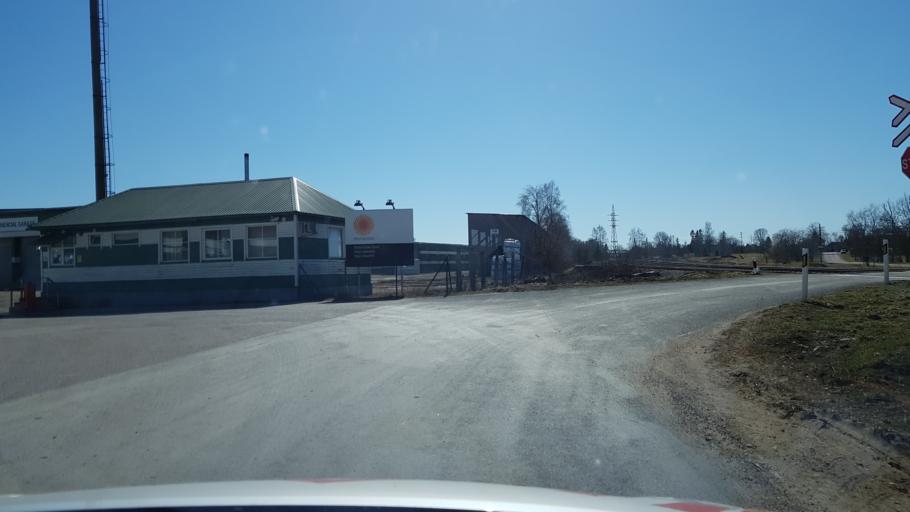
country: EE
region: Laeaene-Virumaa
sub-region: Someru vald
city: Someru
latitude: 59.3633
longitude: 26.3953
